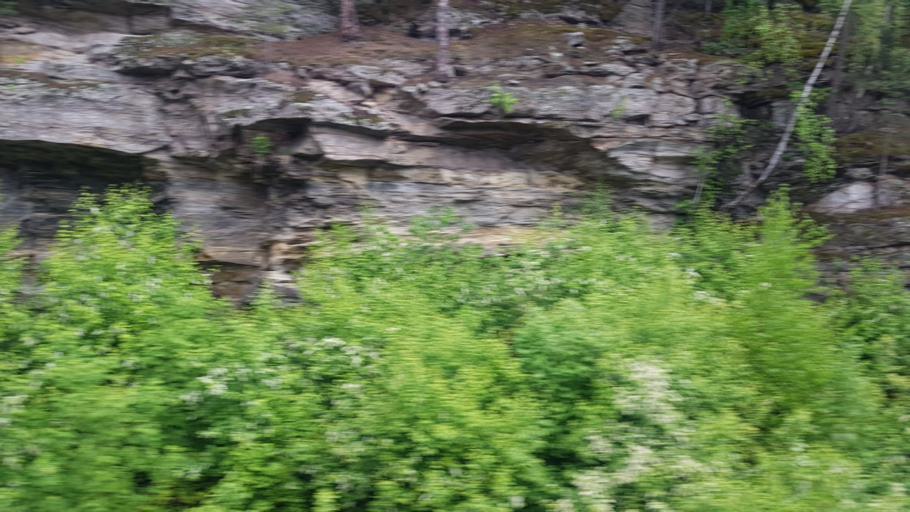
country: NO
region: Oppland
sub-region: Sor-Fron
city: Hundorp
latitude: 61.5664
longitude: 9.9160
